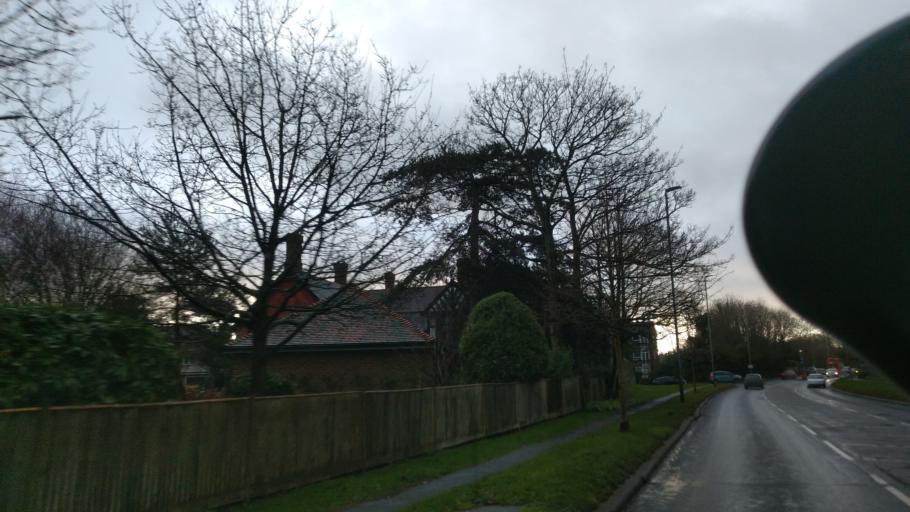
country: GB
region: England
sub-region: East Sussex
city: Eastbourne
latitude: 50.7922
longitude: 0.2563
